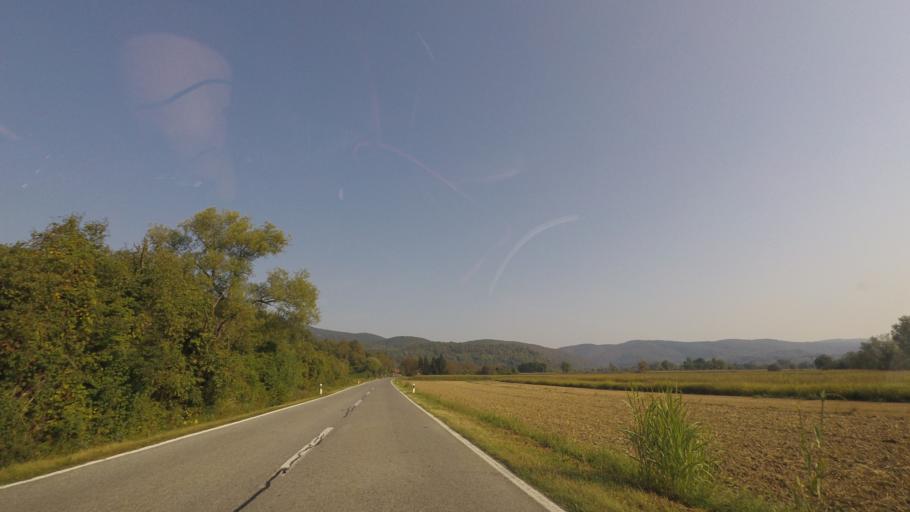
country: HR
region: Brodsko-Posavska
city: Resetari
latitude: 45.4063
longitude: 17.5002
